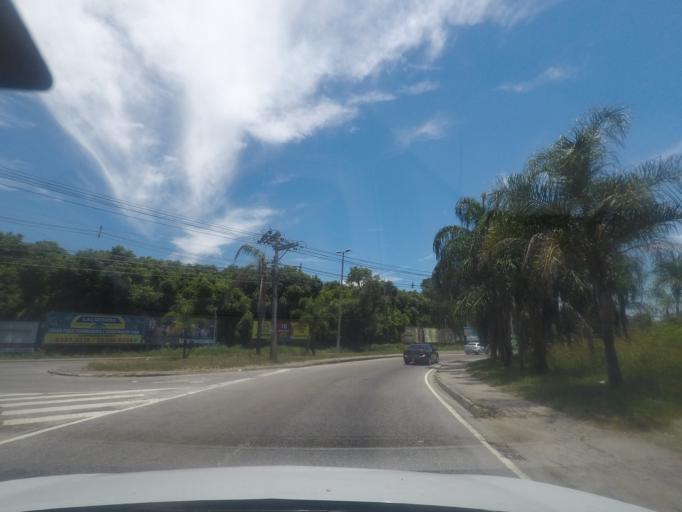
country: BR
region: Rio de Janeiro
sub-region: Itaguai
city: Itaguai
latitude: -22.8948
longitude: -43.6764
